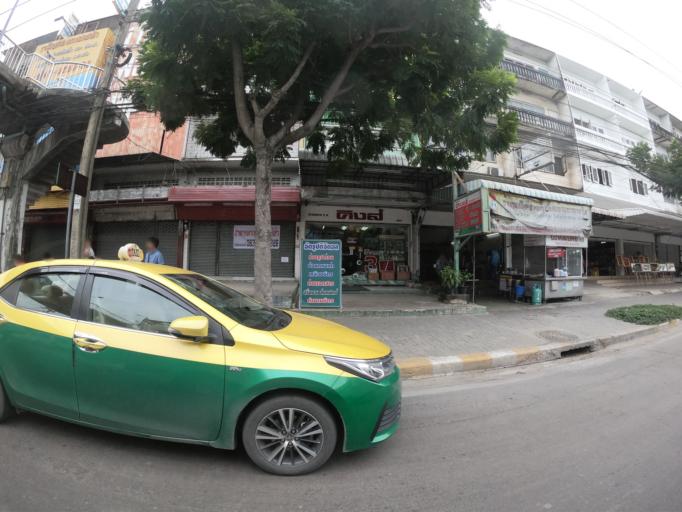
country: TH
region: Bangkok
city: Bang Na
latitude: 13.6773
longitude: 100.6625
